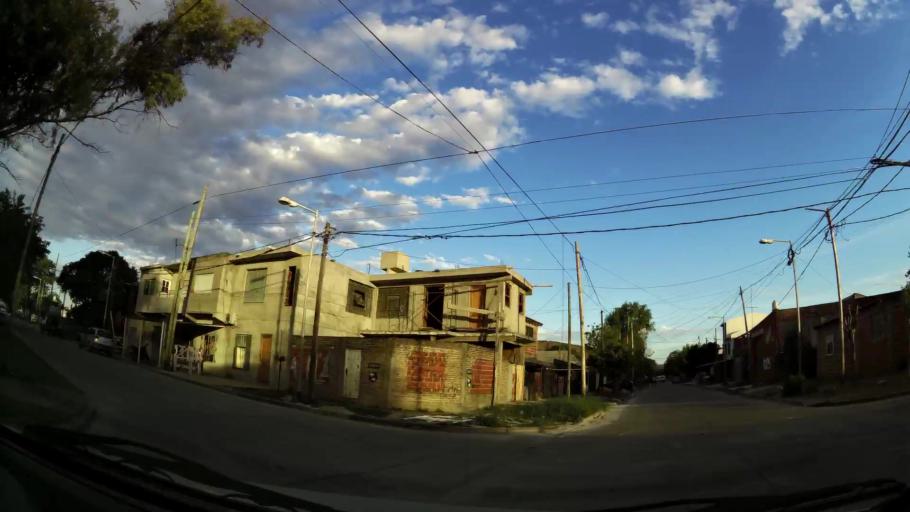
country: AR
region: Buenos Aires
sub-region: Partido de Avellaneda
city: Avellaneda
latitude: -34.7050
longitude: -58.3410
